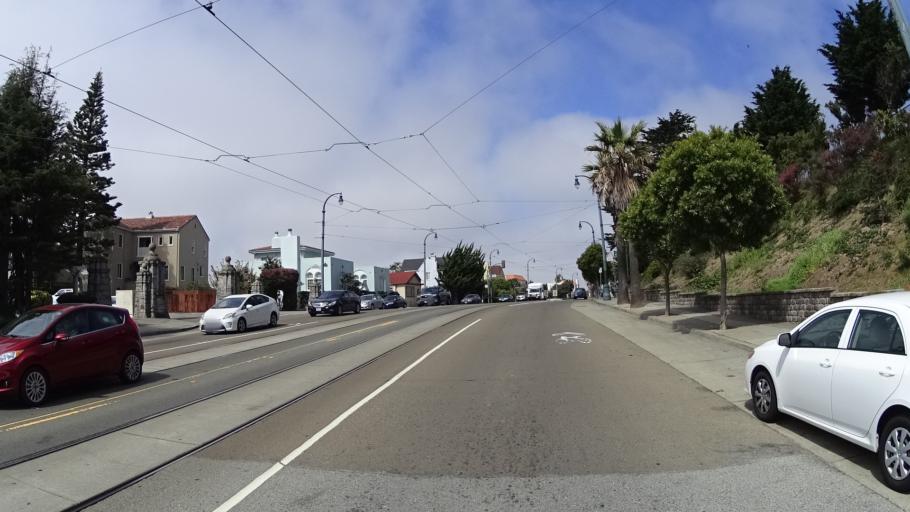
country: US
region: California
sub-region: San Mateo County
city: Daly City
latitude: 37.7276
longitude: -122.4670
